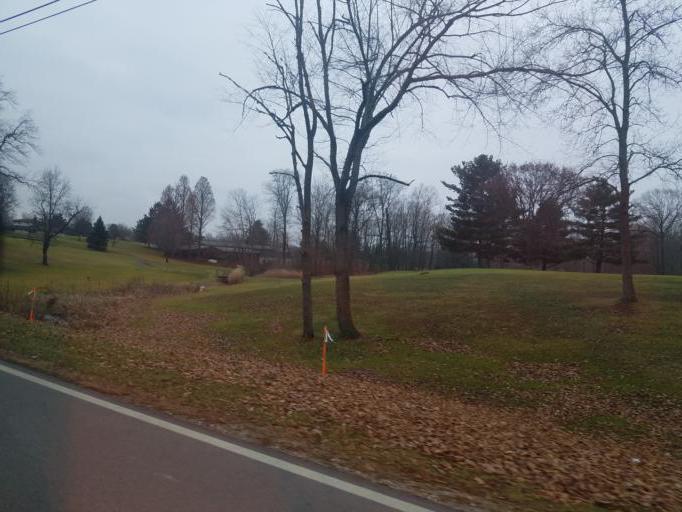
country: US
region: Ohio
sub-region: Delaware County
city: Sunbury
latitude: 40.2167
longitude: -82.8942
